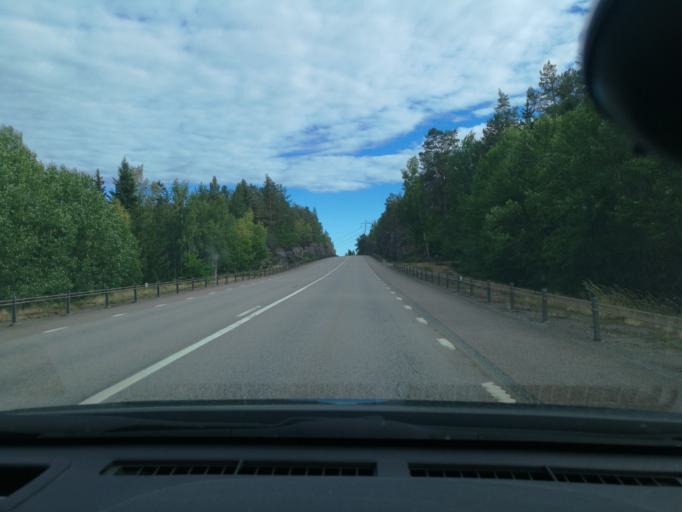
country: SE
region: Kalmar
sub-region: Vasterviks Kommun
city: Ankarsrum
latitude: 57.5396
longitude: 16.4812
